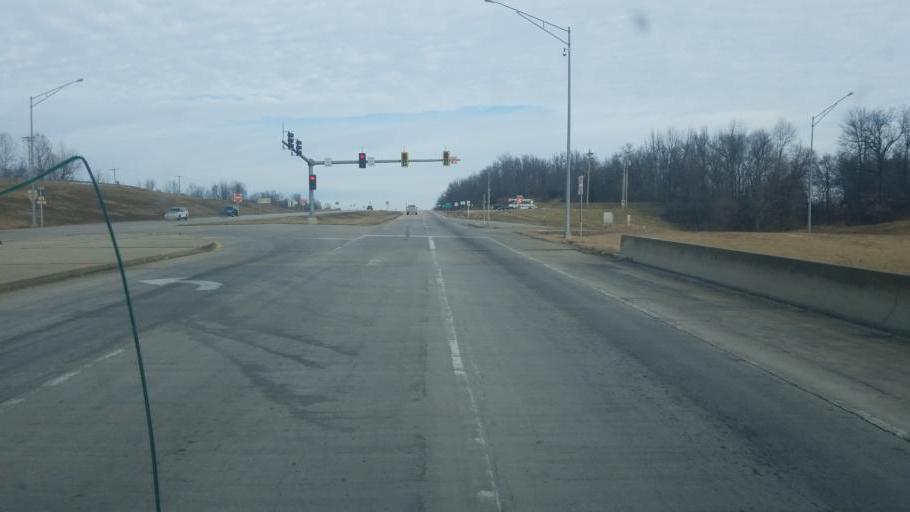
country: US
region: Missouri
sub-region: Stoddard County
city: Dexter
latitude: 36.8165
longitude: -89.9416
